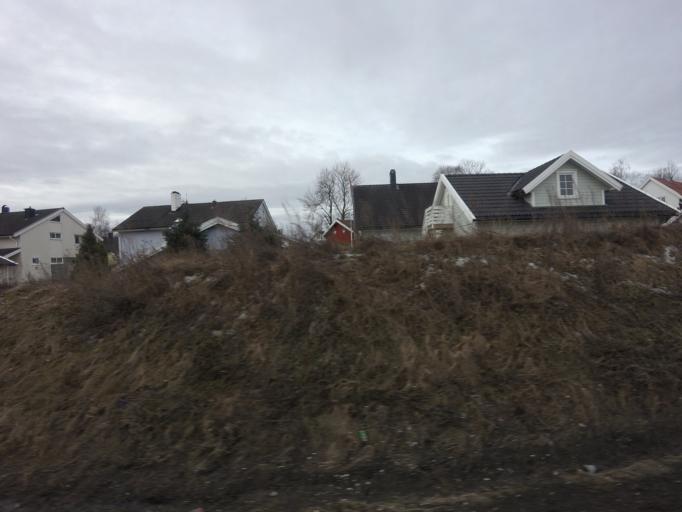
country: NO
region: Akershus
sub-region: Skedsmo
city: Lillestrom
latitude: 59.9958
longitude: 11.0465
